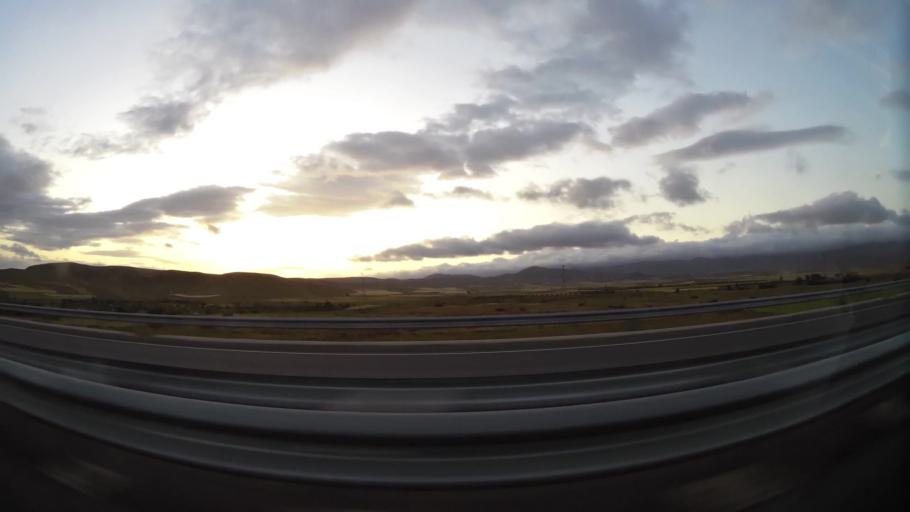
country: MA
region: Oriental
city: El Aioun
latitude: 34.6208
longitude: -2.5478
